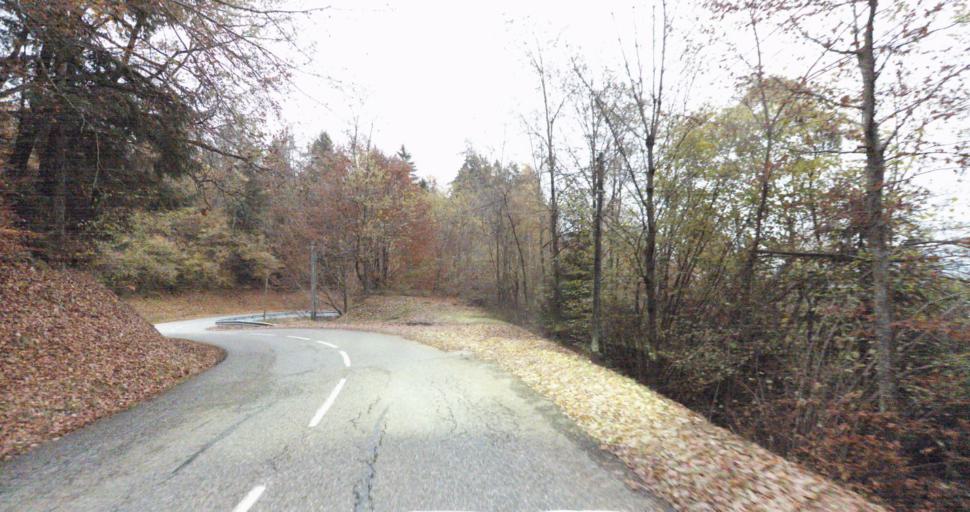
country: FR
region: Rhone-Alpes
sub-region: Departement de la Haute-Savoie
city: Saint-Jorioz
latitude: 45.7986
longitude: 6.1378
